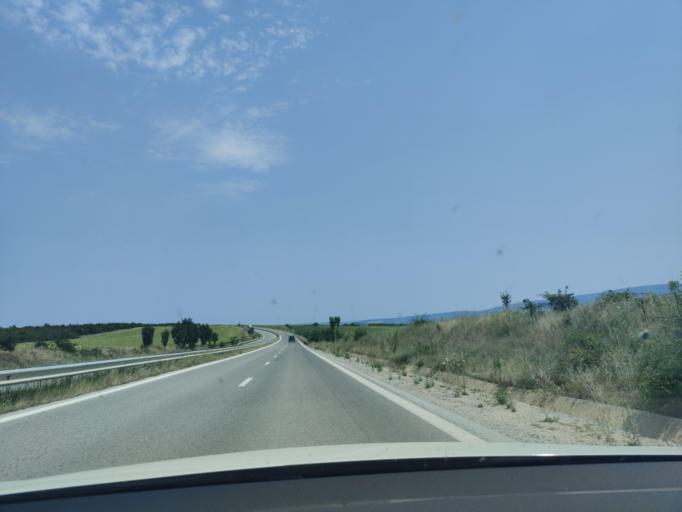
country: BG
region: Montana
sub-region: Obshtina Montana
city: Montana
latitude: 43.4356
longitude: 23.1915
